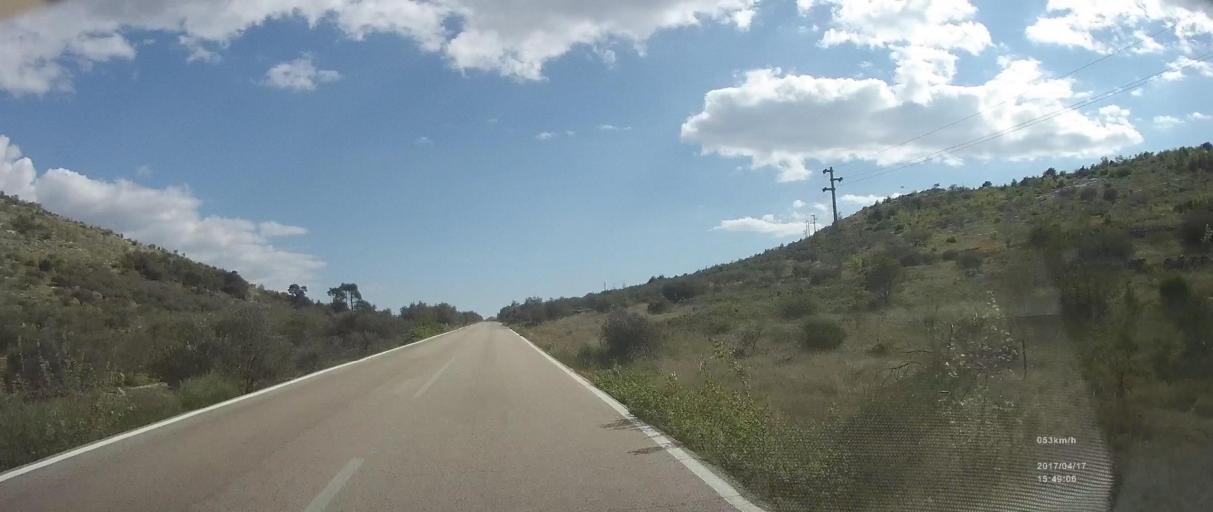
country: HR
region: Sibensko-Kniniska
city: Primosten
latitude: 43.6169
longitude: 15.9764
